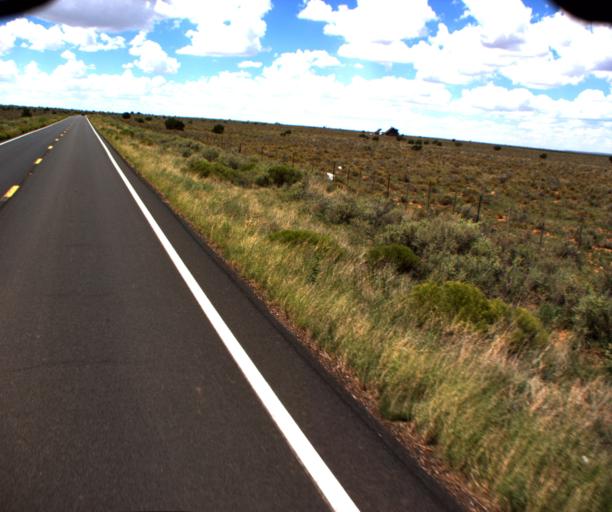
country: US
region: Arizona
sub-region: Coconino County
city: Williams
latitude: 35.6202
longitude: -112.1001
